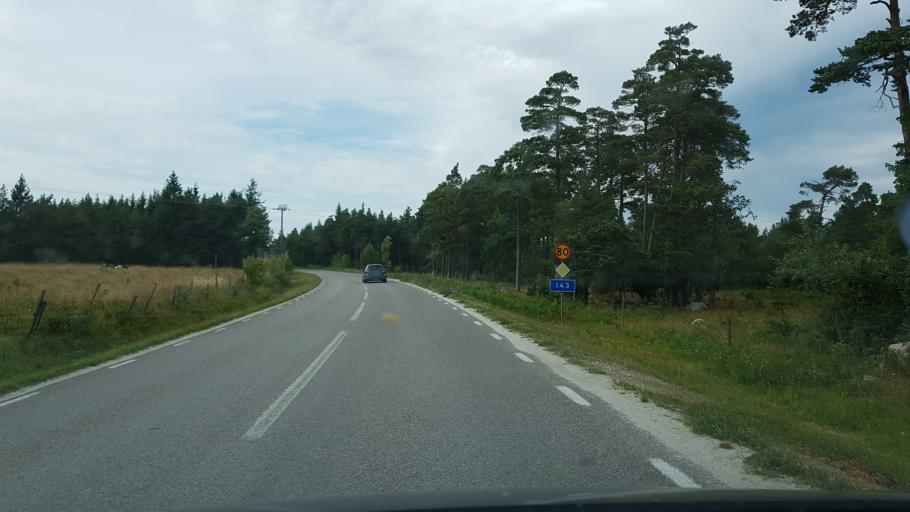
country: SE
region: Gotland
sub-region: Gotland
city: Hemse
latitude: 57.3620
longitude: 18.6840
